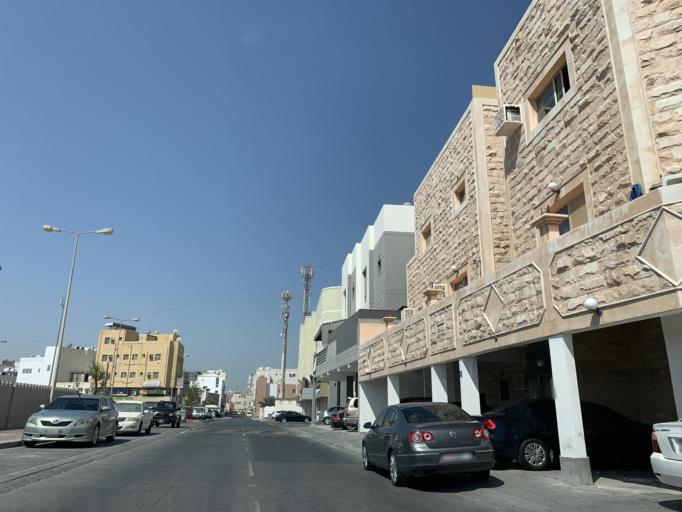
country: BH
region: Muharraq
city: Al Muharraq
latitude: 26.2699
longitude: 50.6114
